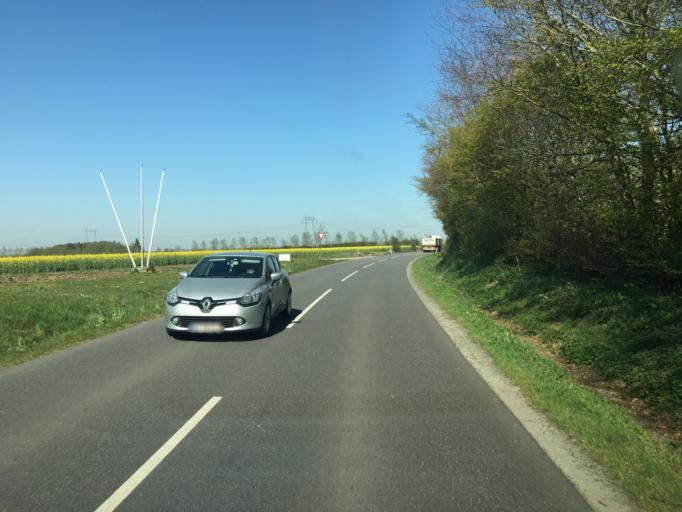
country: DK
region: South Denmark
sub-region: Aabenraa Kommune
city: Tinglev
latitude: 54.9949
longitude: 9.2943
